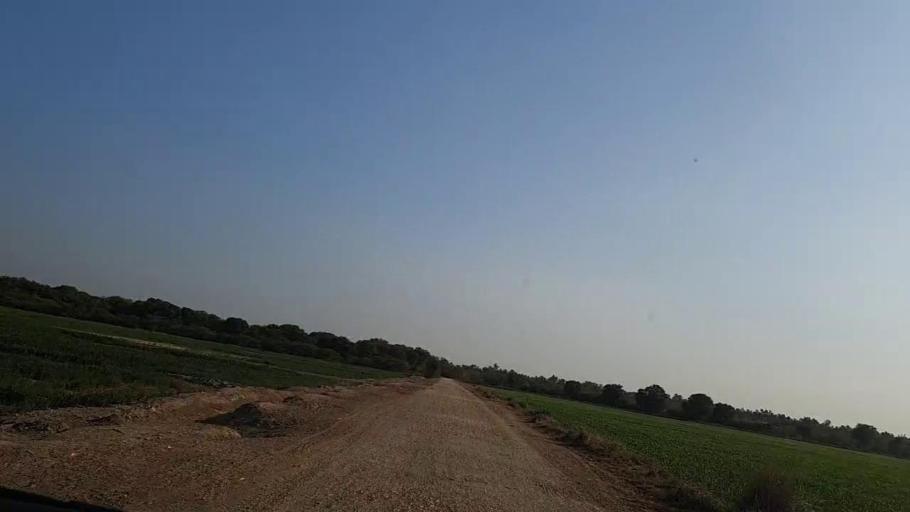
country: PK
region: Sindh
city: Sakrand
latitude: 26.0968
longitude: 68.2132
